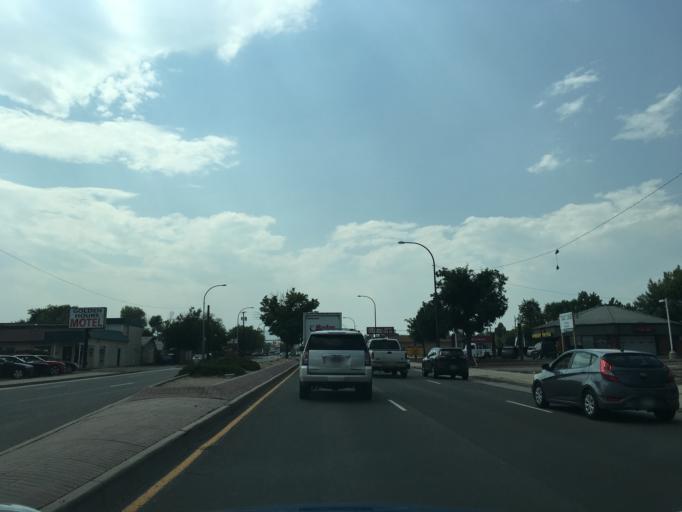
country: US
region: Colorado
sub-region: Jefferson County
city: Applewood
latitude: 39.7402
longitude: -105.1205
